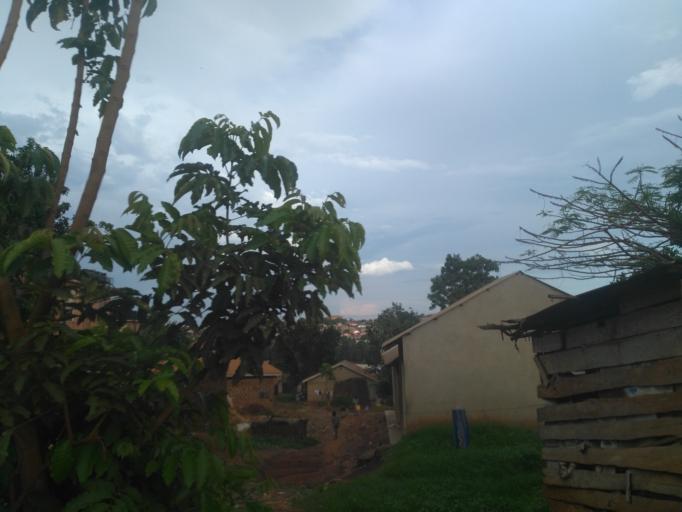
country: UG
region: Central Region
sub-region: Wakiso District
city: Kireka
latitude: 0.3718
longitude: 32.6136
